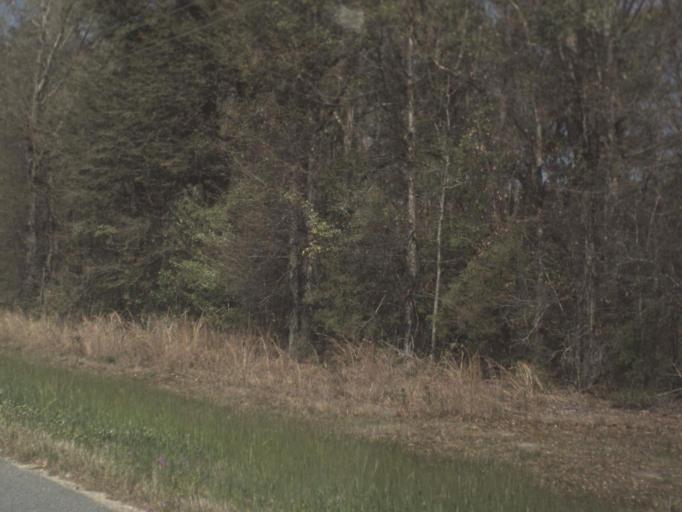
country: US
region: Florida
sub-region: Jackson County
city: Graceville
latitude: 30.9725
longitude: -85.6149
